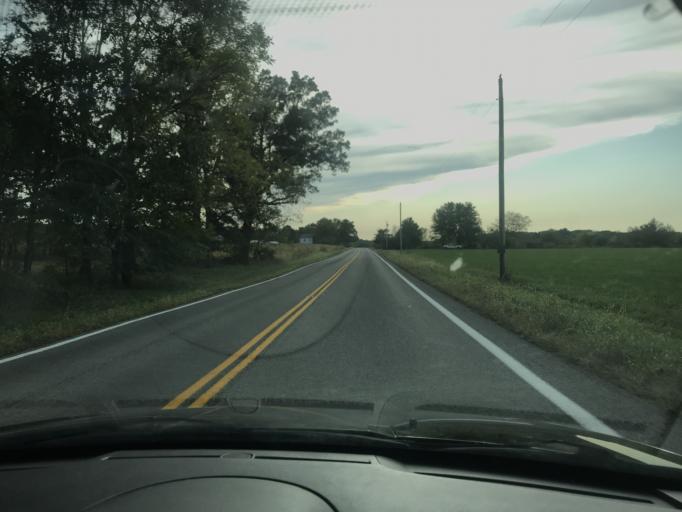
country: US
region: Ohio
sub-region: Logan County
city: West Liberty
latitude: 40.2629
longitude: -83.6938
